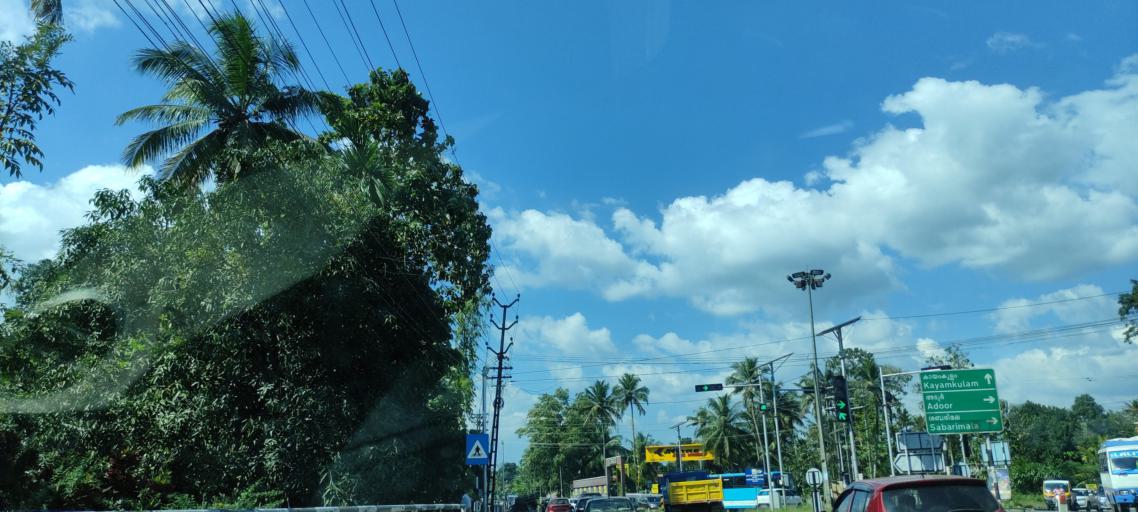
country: IN
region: Kerala
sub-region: Pattanamtitta
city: Adur
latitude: 9.1458
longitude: 76.7322
